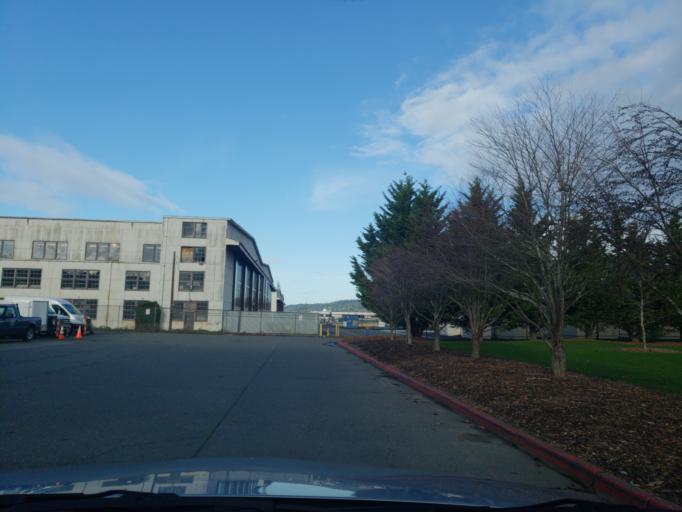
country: US
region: Washington
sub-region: King County
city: Inglewood-Finn Hill
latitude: 47.6831
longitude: -122.2604
